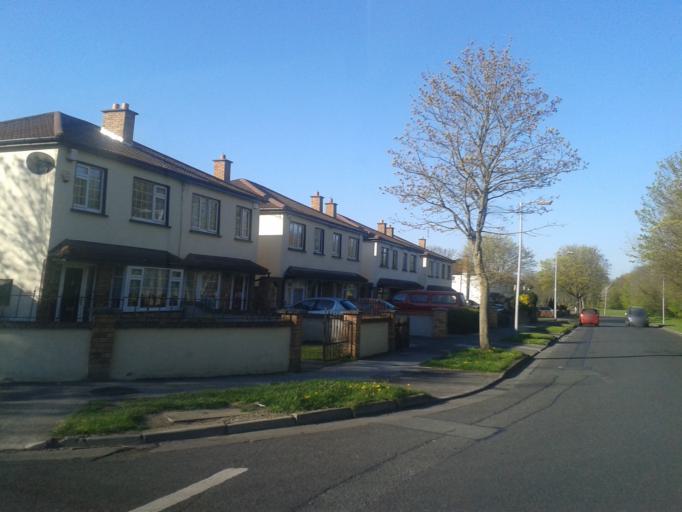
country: IE
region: Leinster
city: Beaumont
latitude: 53.3993
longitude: -6.2379
